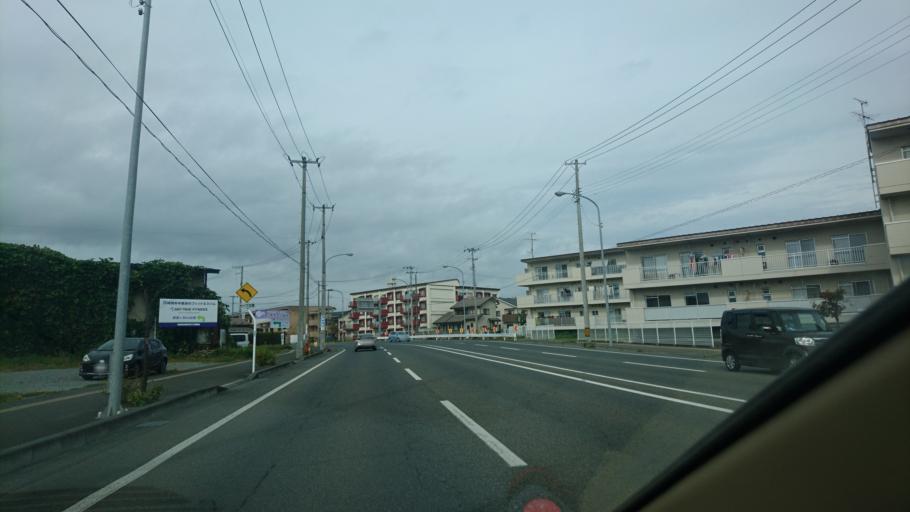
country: JP
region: Iwate
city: Morioka-shi
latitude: 39.6841
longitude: 141.1555
